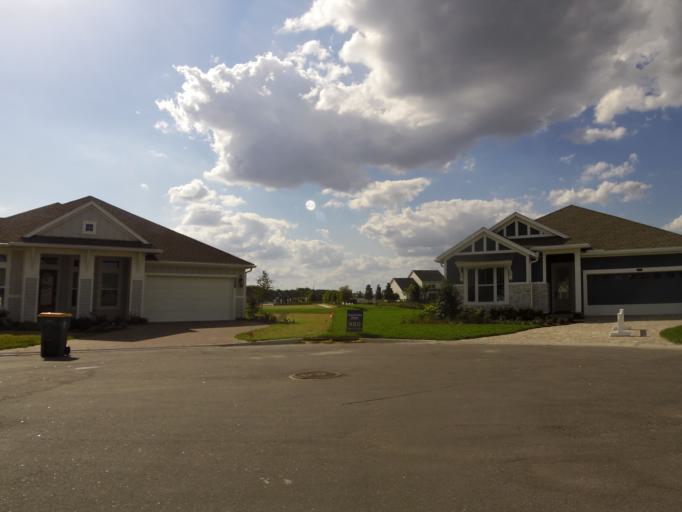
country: US
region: Florida
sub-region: Saint Johns County
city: Palm Valley
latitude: 30.1738
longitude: -81.5036
